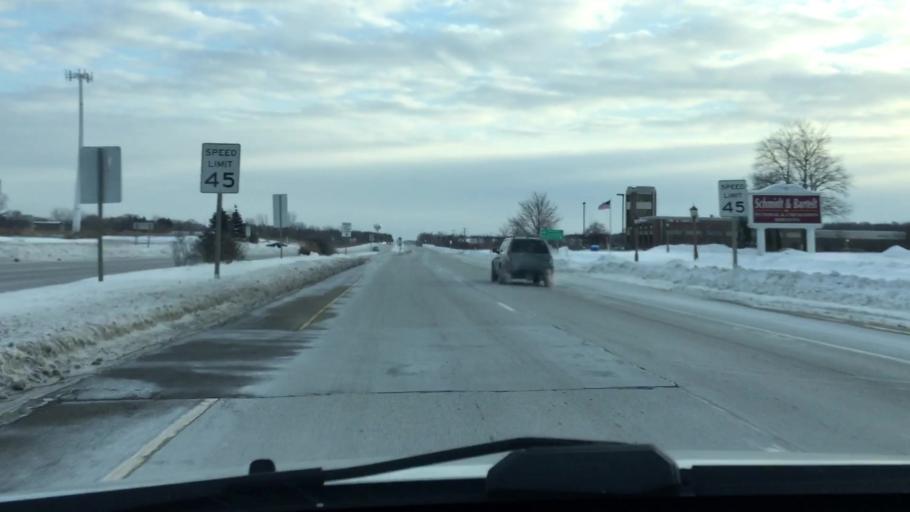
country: US
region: Wisconsin
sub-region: Waukesha County
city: Sussex
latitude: 43.1363
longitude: -88.2440
